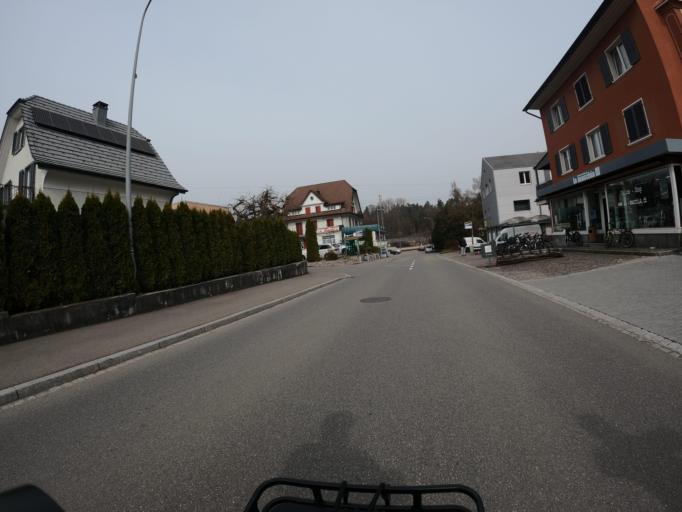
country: CH
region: Aargau
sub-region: Bezirk Lenzburg
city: Othmarsingen
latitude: 47.4066
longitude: 8.2152
